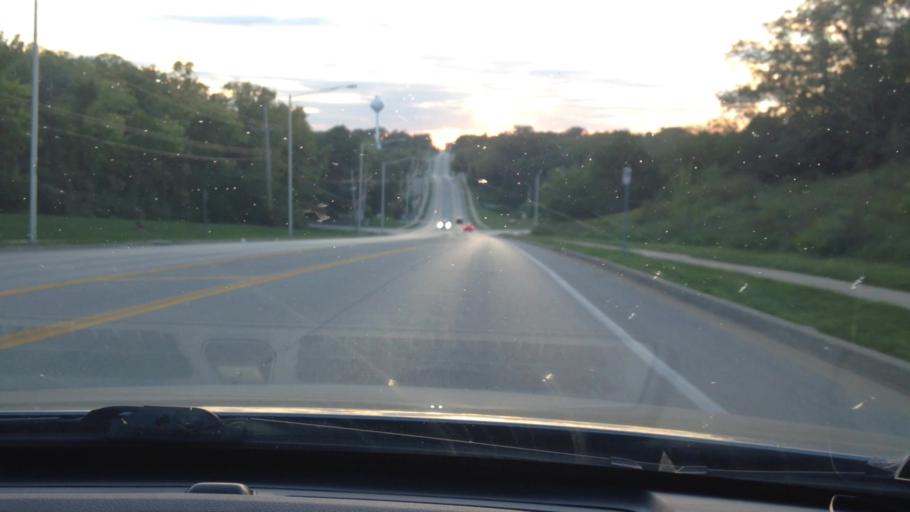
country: US
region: Missouri
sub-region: Platte County
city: Weatherby Lake
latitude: 39.2471
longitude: -94.6841
